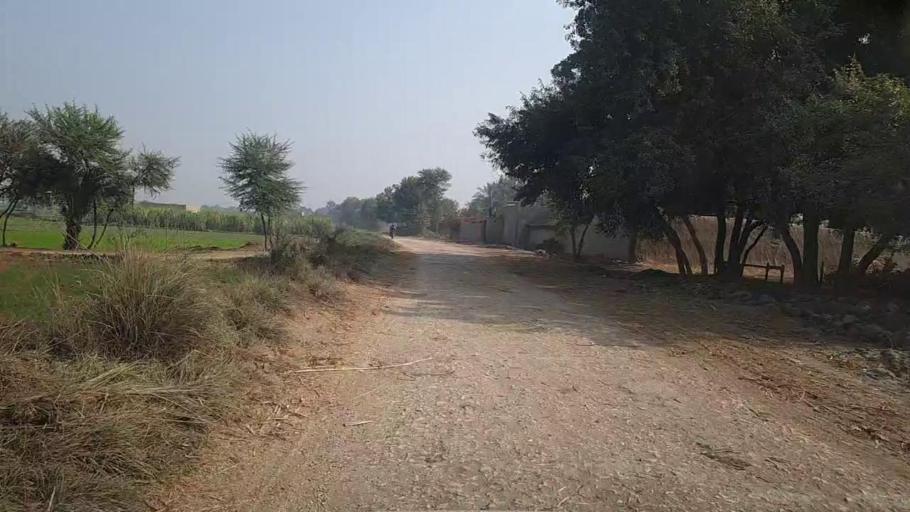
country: PK
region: Sindh
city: Setharja Old
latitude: 27.1306
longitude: 68.5132
